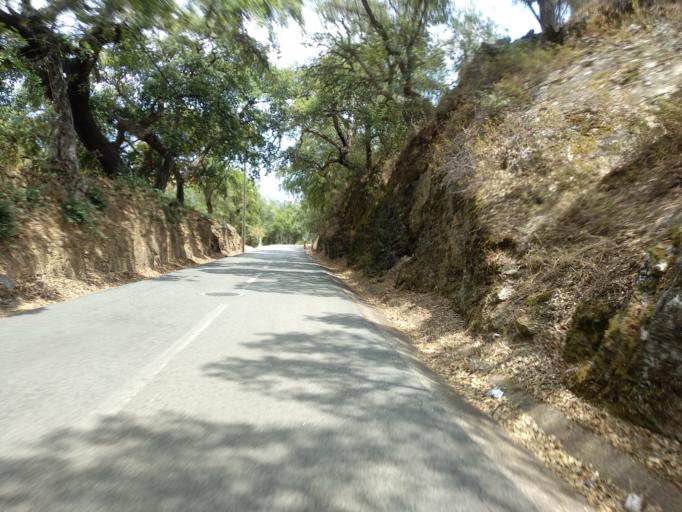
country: PT
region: Faro
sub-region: Sao Bras de Alportel
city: Sao Bras de Alportel
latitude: 37.1633
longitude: -7.8903
